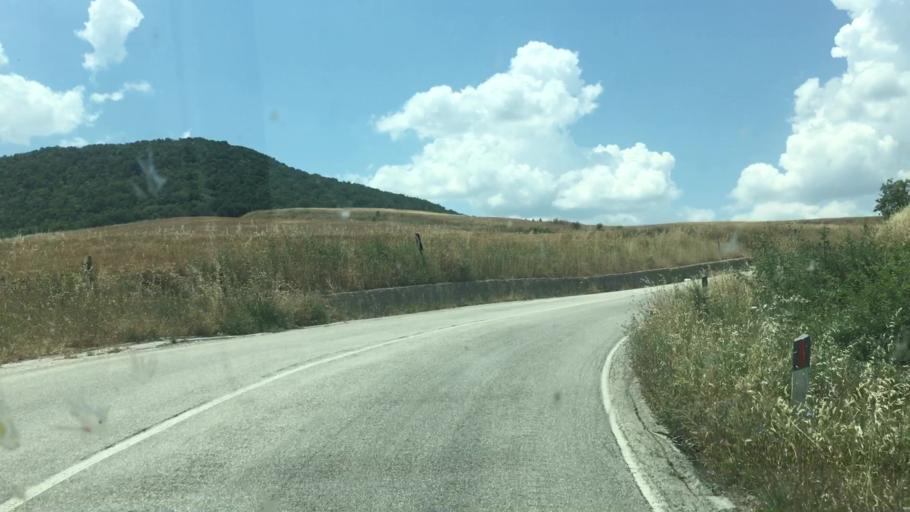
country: IT
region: Basilicate
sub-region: Provincia di Potenza
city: Tolve
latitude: 40.6898
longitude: 15.9866
